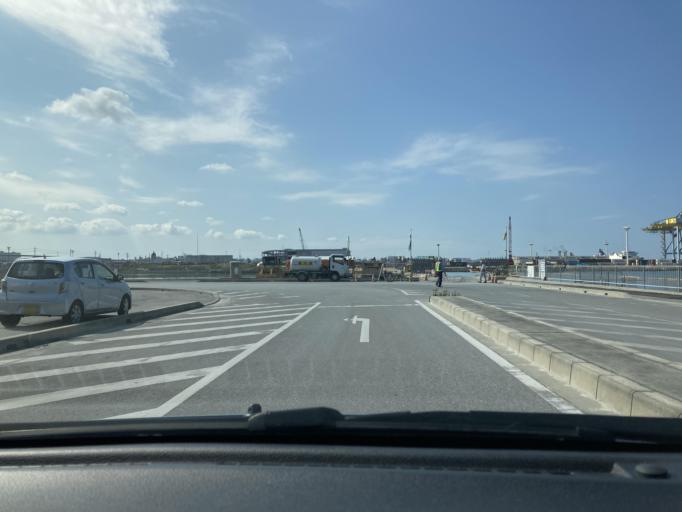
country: JP
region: Okinawa
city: Naha-shi
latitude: 26.2417
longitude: 127.6707
